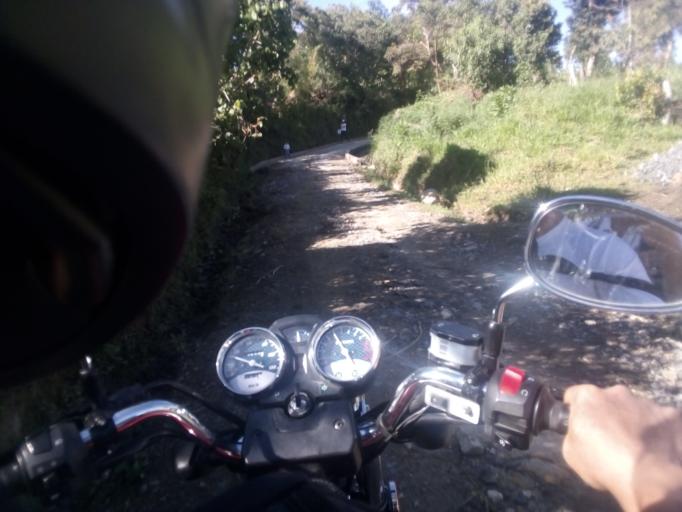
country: CO
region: Santander
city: Guepsa
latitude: 5.9984
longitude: -73.5547
